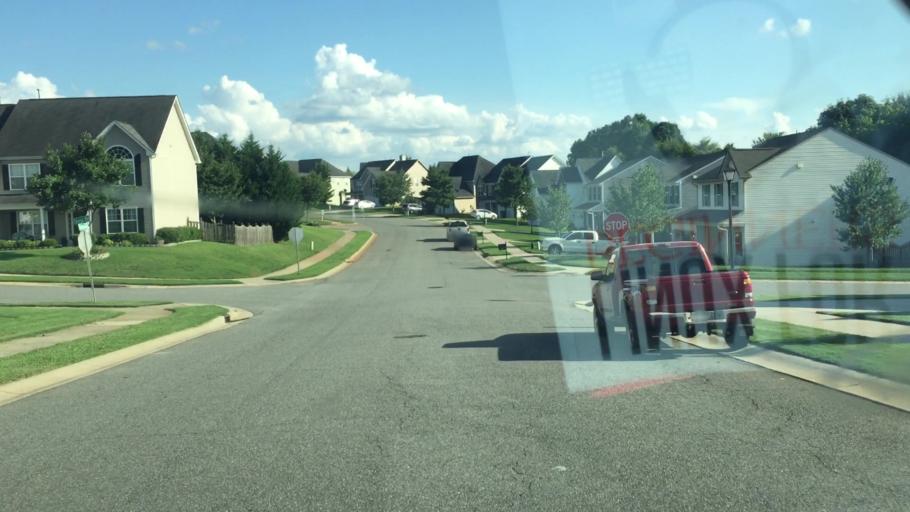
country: US
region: North Carolina
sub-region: Iredell County
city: Mooresville
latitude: 35.5373
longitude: -80.7851
